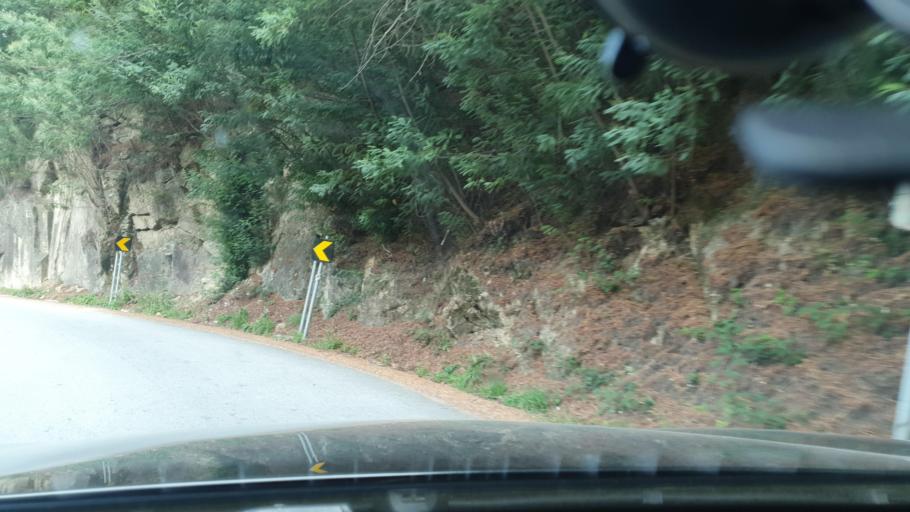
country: PT
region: Braga
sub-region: Vieira do Minho
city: Vieira do Minho
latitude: 41.6869
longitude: -8.0907
